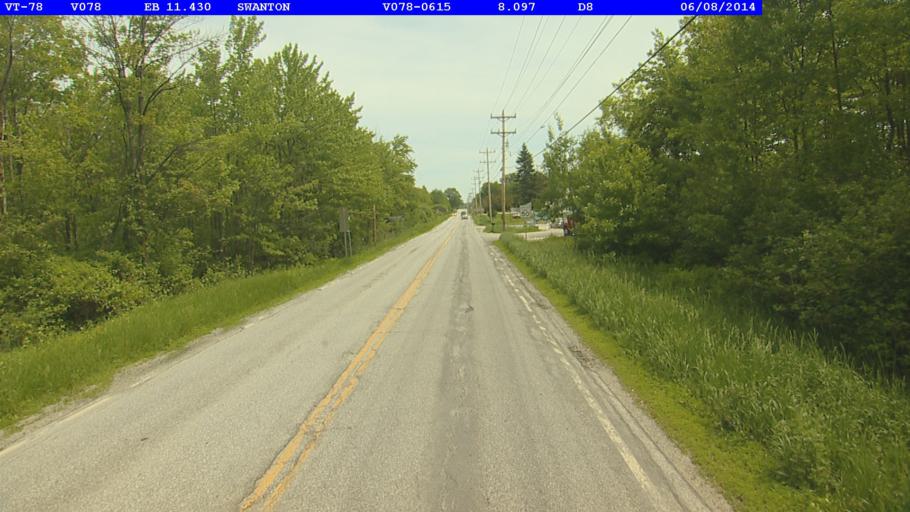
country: US
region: Vermont
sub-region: Franklin County
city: Swanton
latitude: 44.9254
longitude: -73.0989
